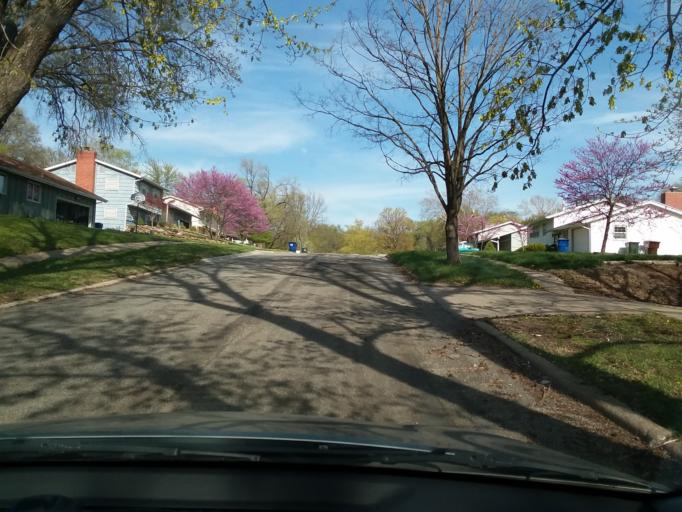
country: US
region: Kansas
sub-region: Douglas County
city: Lawrence
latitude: 38.9690
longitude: -95.2743
